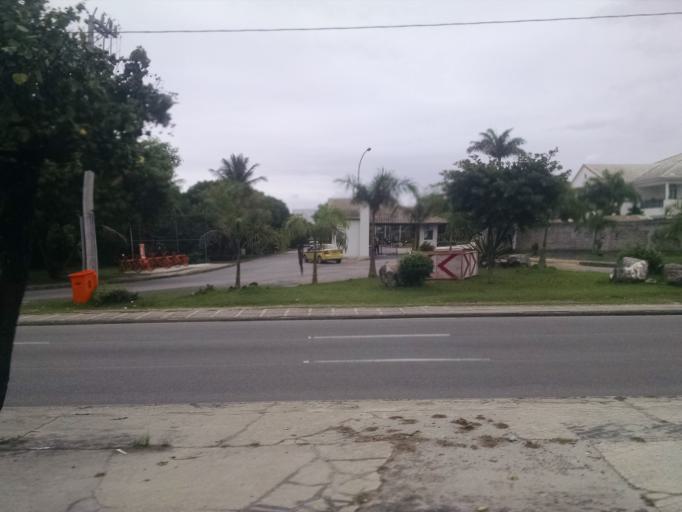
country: BR
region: Rio de Janeiro
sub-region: Rio De Janeiro
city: Rio de Janeiro
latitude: -23.0048
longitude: -43.3661
